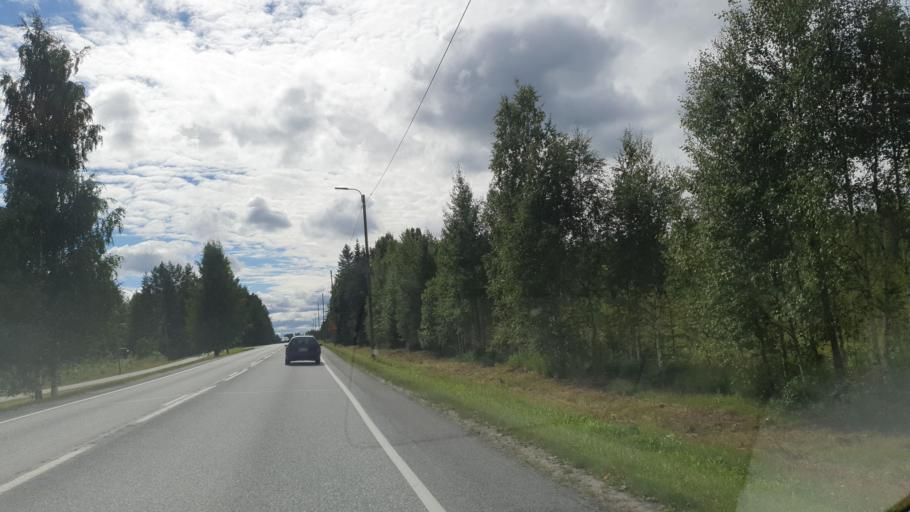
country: FI
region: Kainuu
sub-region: Kajaani
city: Kajaani
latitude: 64.2017
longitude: 27.6393
